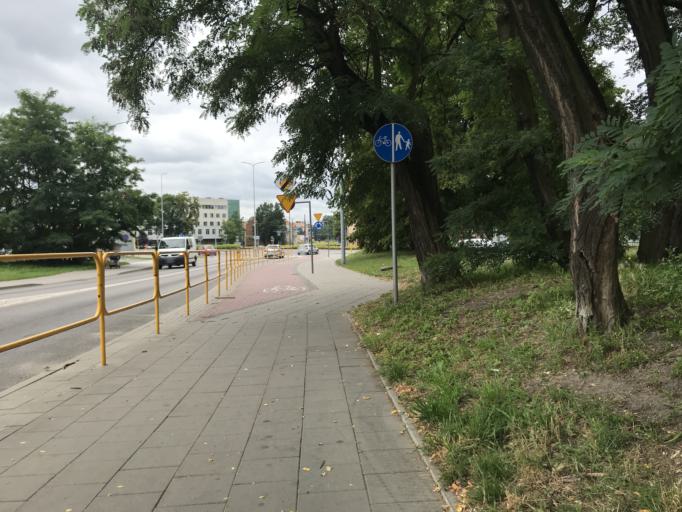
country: PL
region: Warmian-Masurian Voivodeship
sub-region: Powiat elblaski
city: Elblag
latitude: 54.1668
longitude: 19.3998
